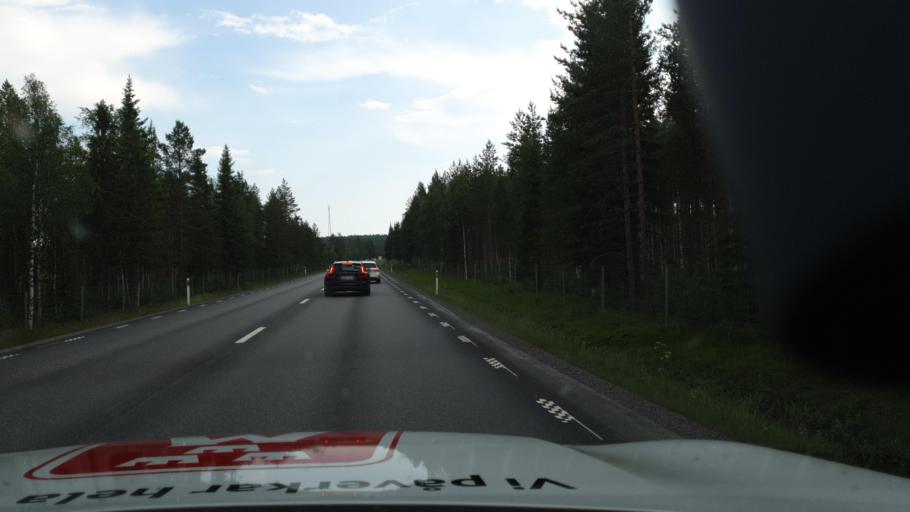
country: SE
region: Vaesterbotten
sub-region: Skelleftea Kommun
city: Burea
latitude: 64.4743
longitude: 21.2909
